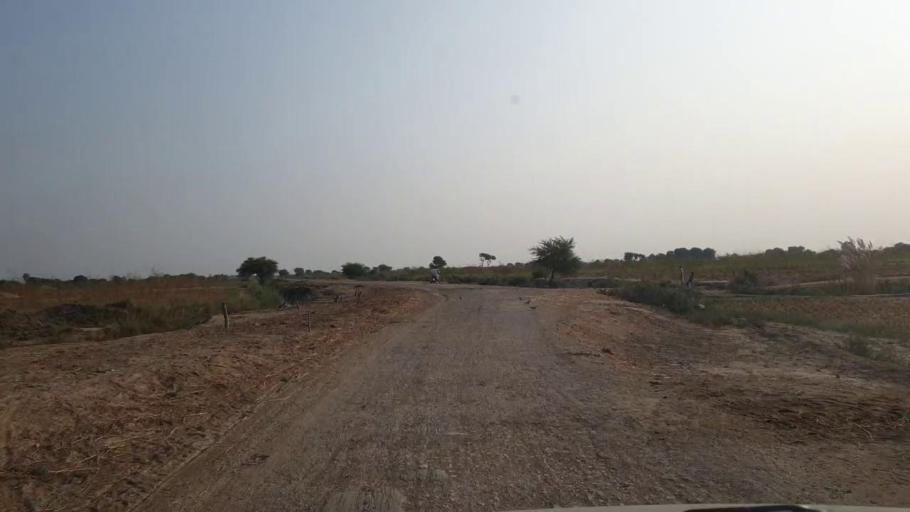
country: PK
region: Sindh
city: Matli
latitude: 25.0595
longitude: 68.7618
